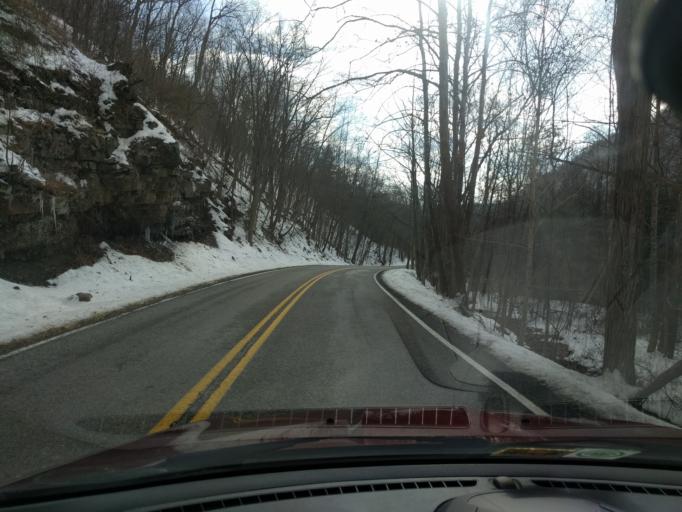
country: US
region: Virginia
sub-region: Bath County
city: Warm Springs
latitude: 38.1111
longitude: -79.9100
